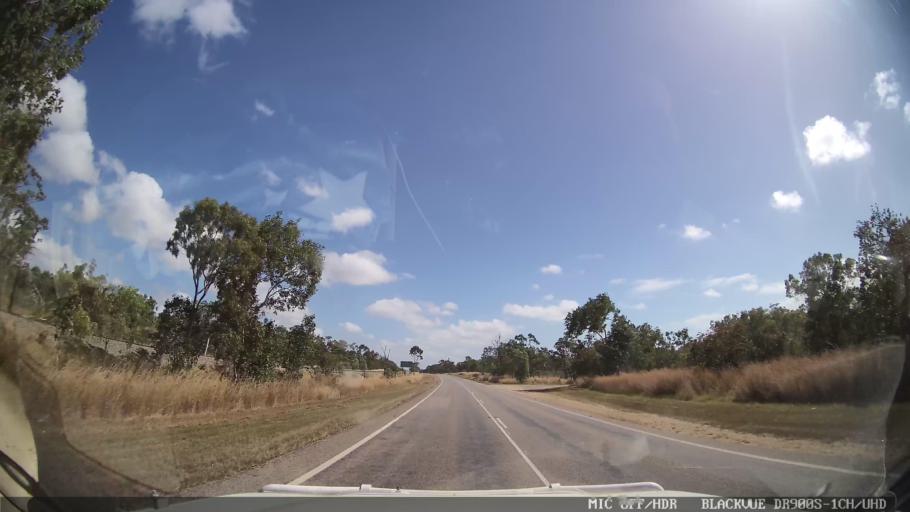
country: AU
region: Queensland
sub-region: Whitsunday
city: Bowen
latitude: -20.1781
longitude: 148.3478
